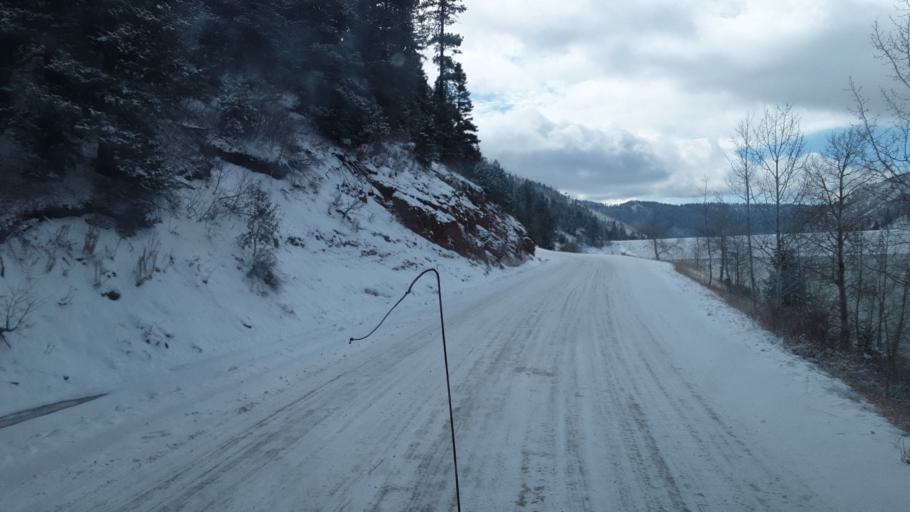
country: US
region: Colorado
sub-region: La Plata County
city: Bayfield
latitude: 37.3903
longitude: -107.6567
